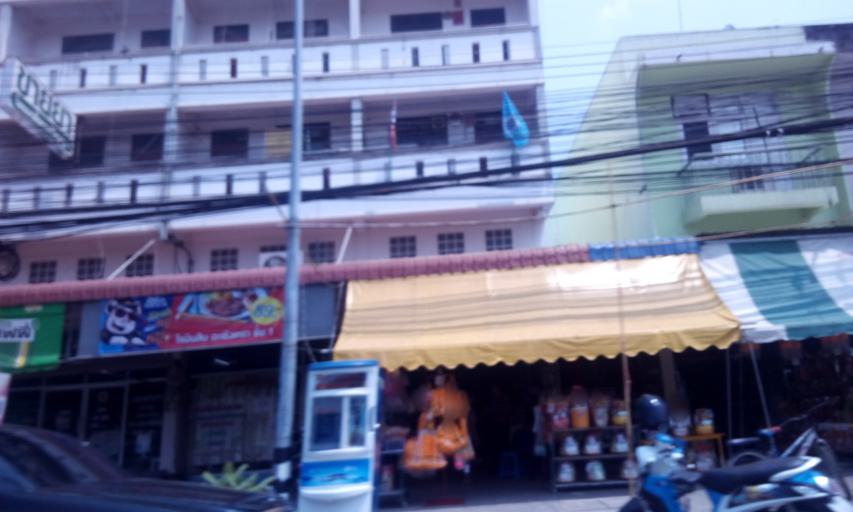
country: TH
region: Chachoengsao
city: Chachoengsao
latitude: 13.7004
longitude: 101.0917
